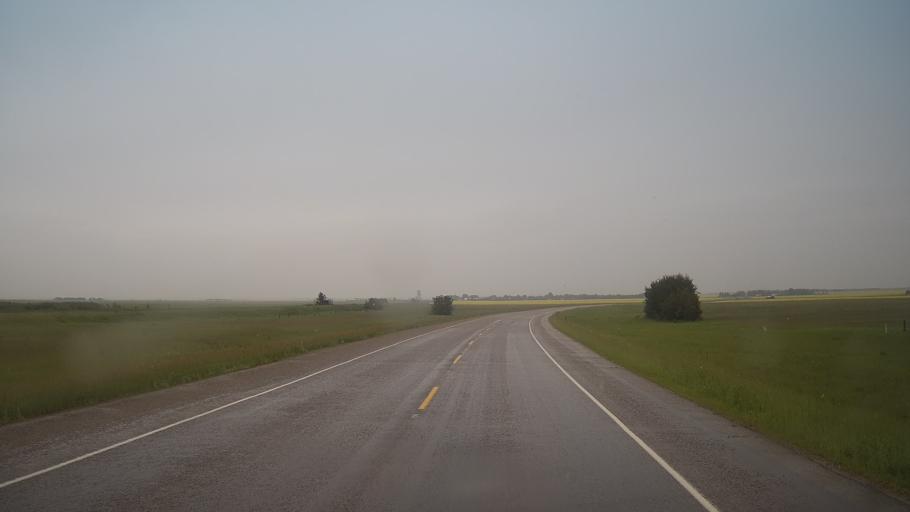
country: CA
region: Saskatchewan
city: Wilkie
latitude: 52.1904
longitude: -108.4188
